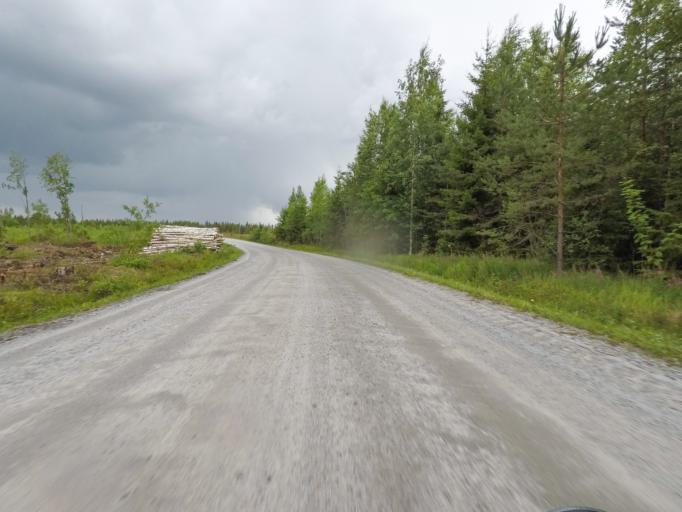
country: FI
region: Central Finland
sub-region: Jyvaeskylae
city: Hankasalmi
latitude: 62.4094
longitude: 26.6056
